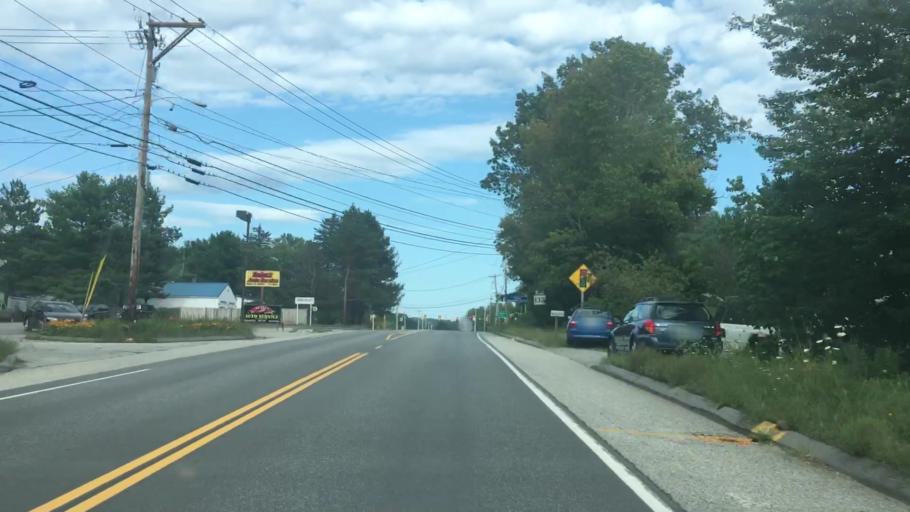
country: US
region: Maine
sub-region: Androscoggin County
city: Sabattus
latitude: 44.1201
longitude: -70.0889
